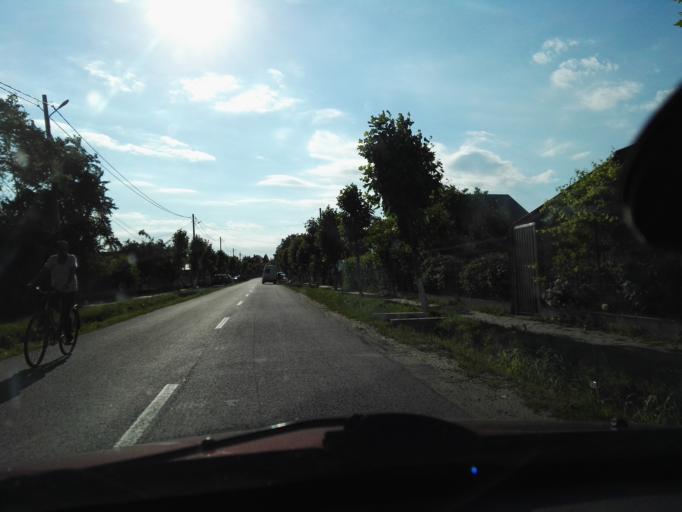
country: RO
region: Giurgiu
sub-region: Comuna Comana
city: Gradistea
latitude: 44.2235
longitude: 26.1488
